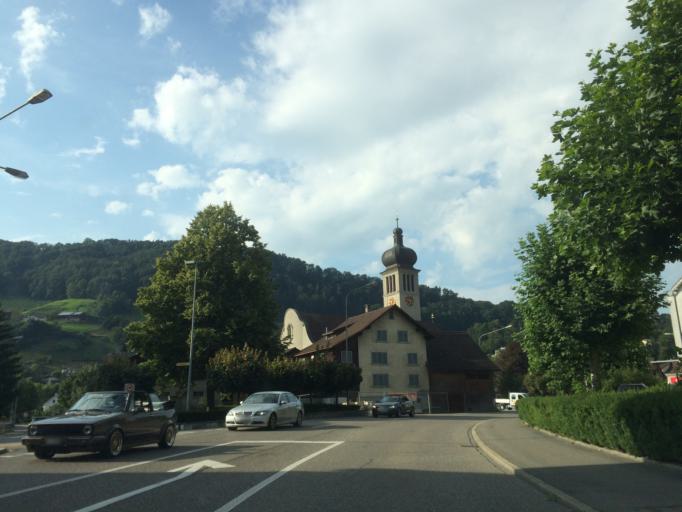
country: CH
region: Saint Gallen
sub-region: Wahlkreis Rheintal
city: Au
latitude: 47.4320
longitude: 9.6340
